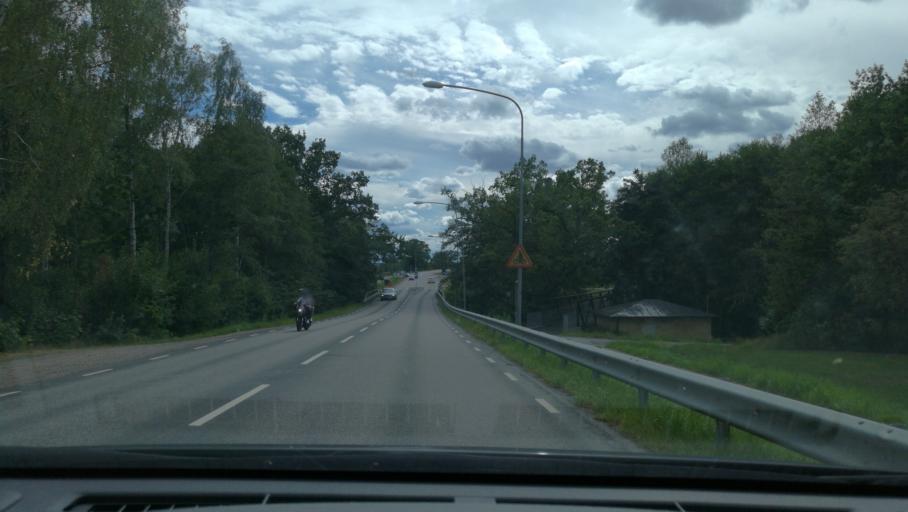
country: SE
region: OEstergoetland
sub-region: Norrkopings Kommun
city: Jursla
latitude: 58.6587
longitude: 16.1738
